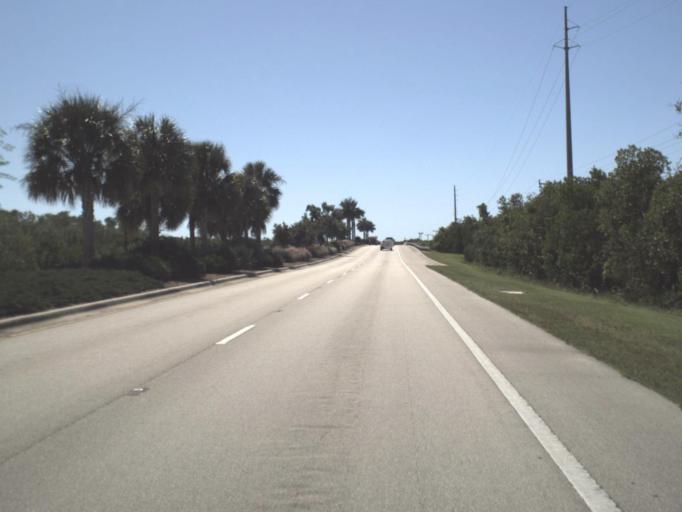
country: US
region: Florida
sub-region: Collier County
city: Marco
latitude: 25.9904
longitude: -81.7022
